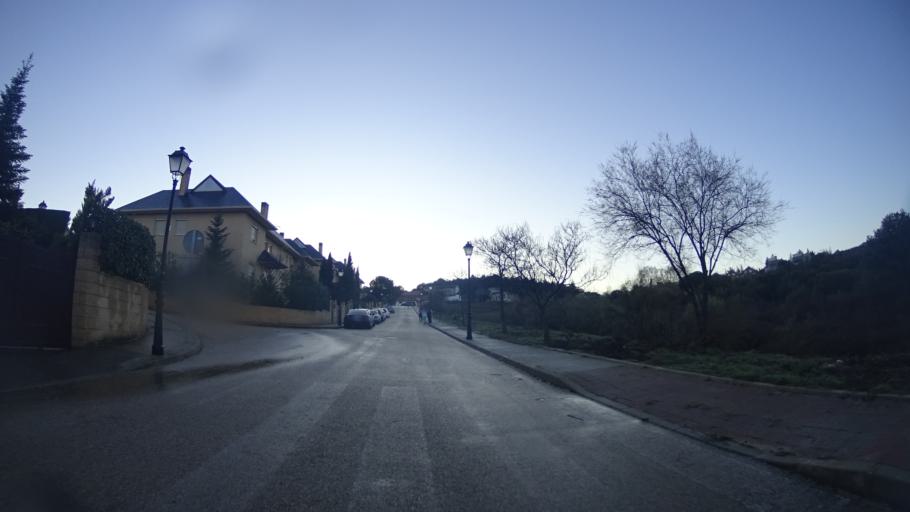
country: ES
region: Madrid
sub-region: Provincia de Madrid
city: Torrelodones
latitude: 40.5767
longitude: -3.9164
